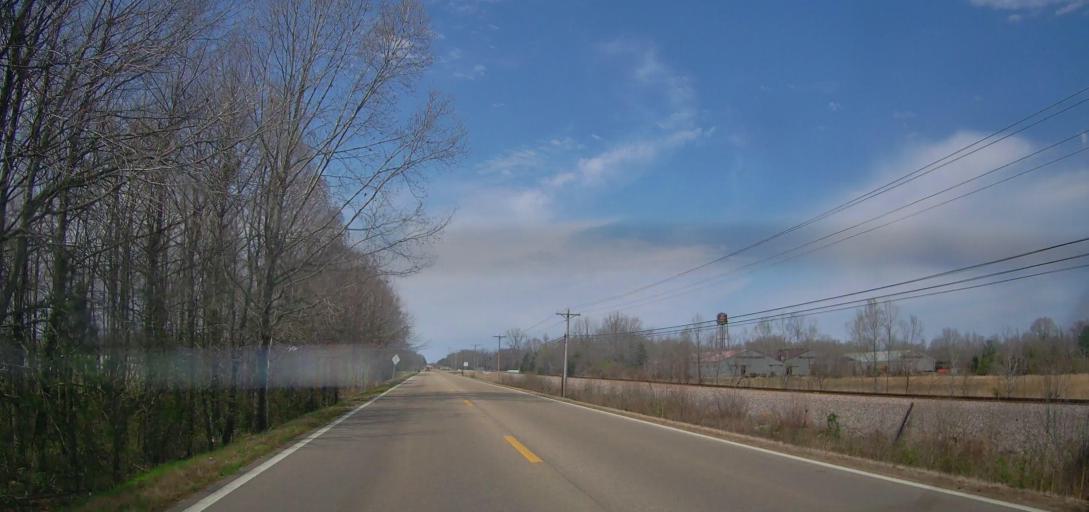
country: US
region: Mississippi
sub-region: Union County
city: New Albany
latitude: 34.5197
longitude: -89.0535
